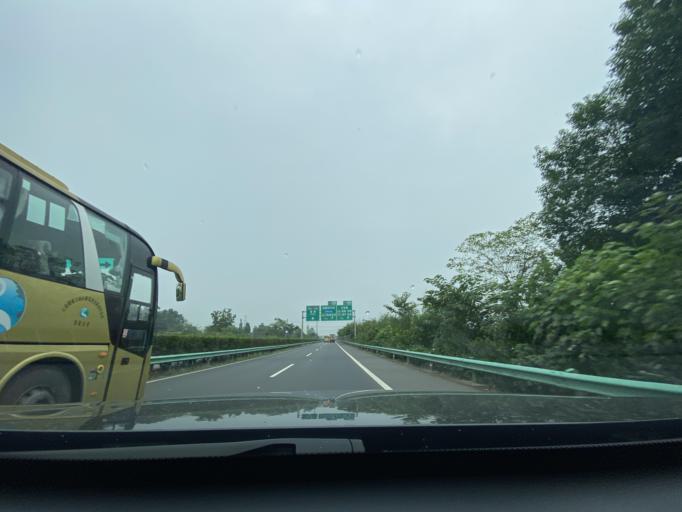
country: CN
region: Sichuan
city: Longquan
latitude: 30.3283
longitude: 104.1203
